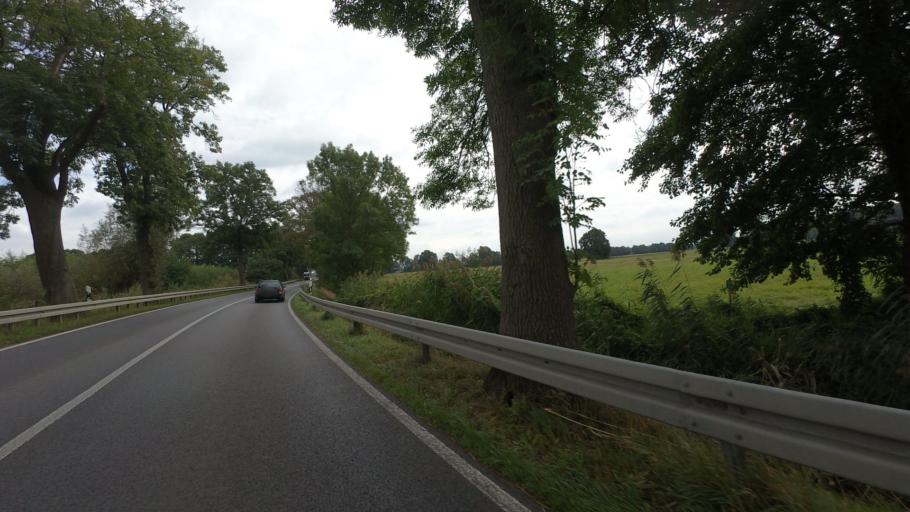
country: DE
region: Brandenburg
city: Golssen
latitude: 51.9628
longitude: 13.6210
